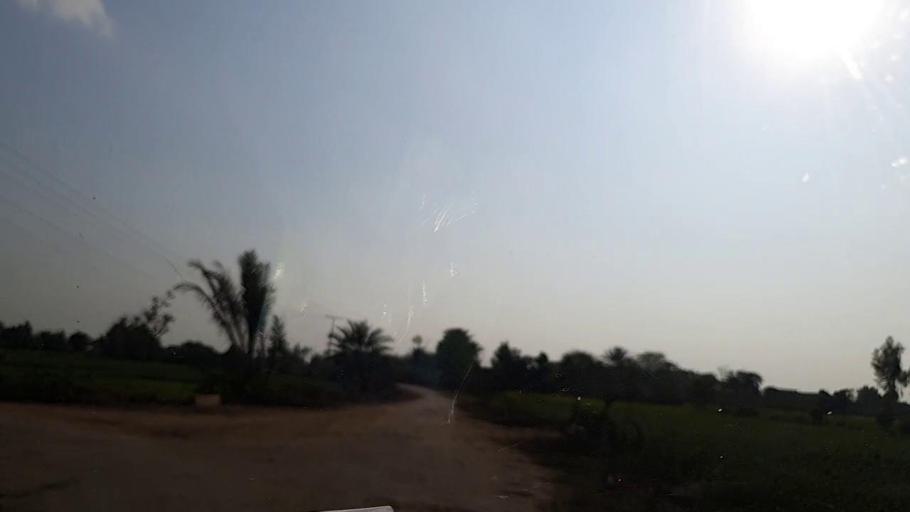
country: PK
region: Sindh
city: Nawabshah
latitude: 26.1454
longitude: 68.3898
